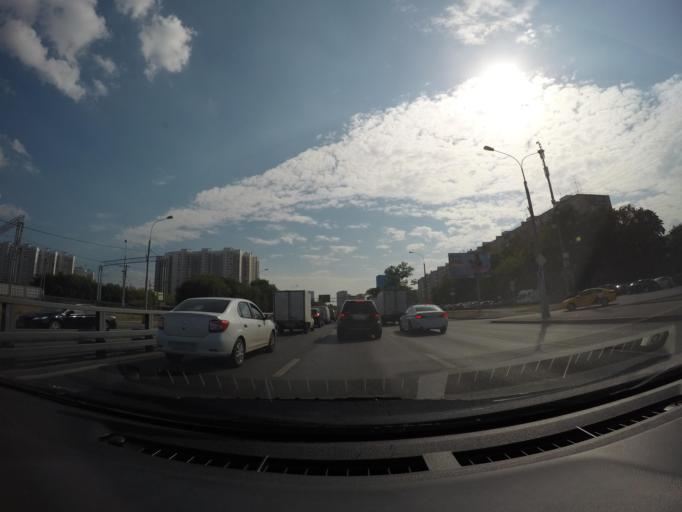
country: RU
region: Moscow
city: Likhobory
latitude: 55.8326
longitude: 37.5728
